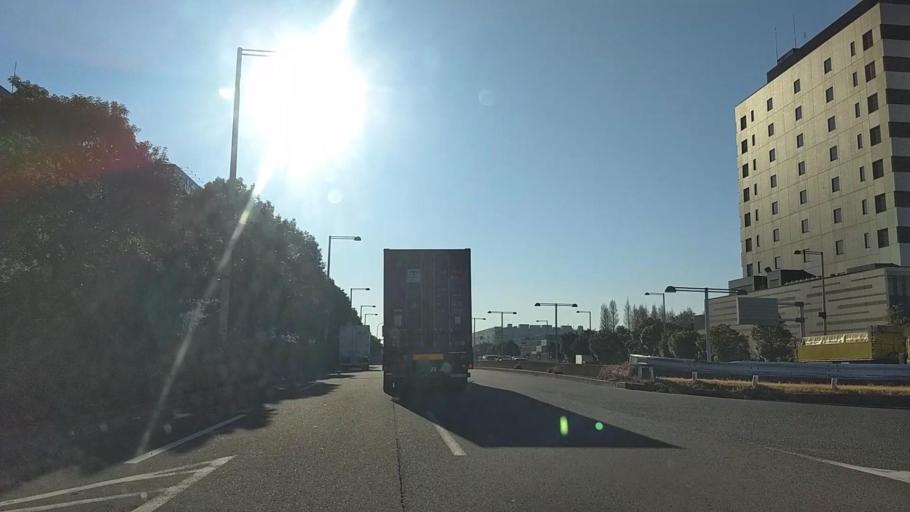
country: JP
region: Tokyo
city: Tokyo
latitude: 35.6178
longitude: 139.7817
